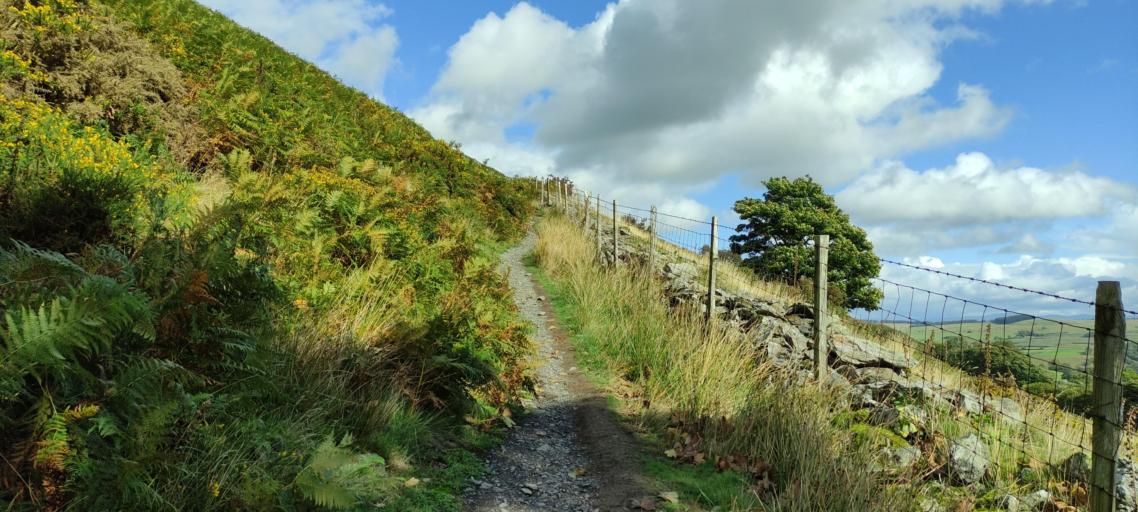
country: GB
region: England
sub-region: Cumbria
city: Keswick
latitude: 54.6341
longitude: -3.0186
